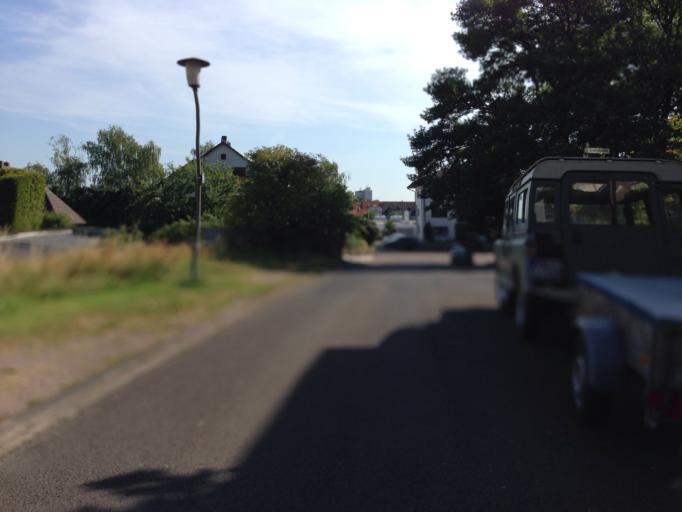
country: DE
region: Hesse
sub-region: Regierungsbezirk Darmstadt
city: Hanau am Main
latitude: 50.1165
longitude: 8.8998
